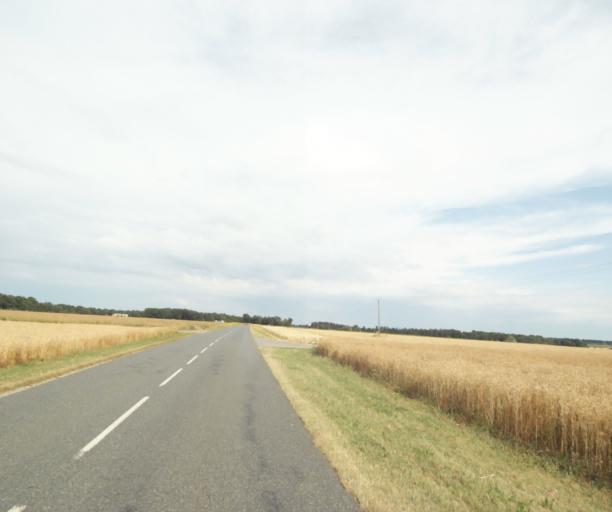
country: FR
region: Ile-de-France
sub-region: Departement de Seine-et-Marne
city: Acheres-la-Foret
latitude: 48.3496
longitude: 2.5806
